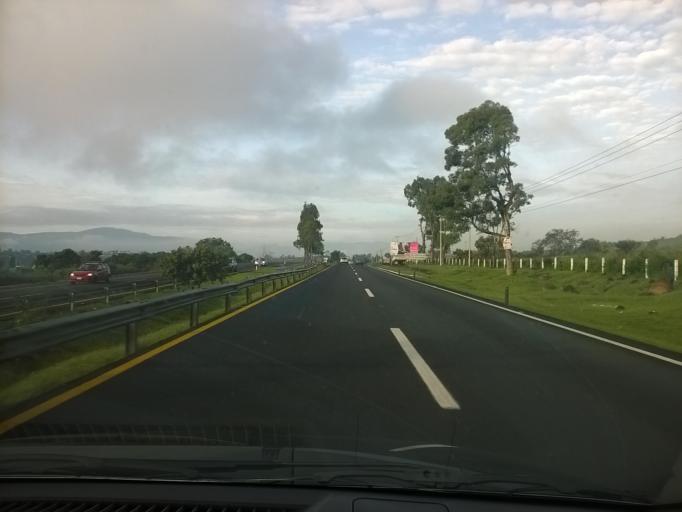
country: MX
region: Michoacan
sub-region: Morelia
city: La Mintzita (Piedra Dura)
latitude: 19.6150
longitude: -101.2836
